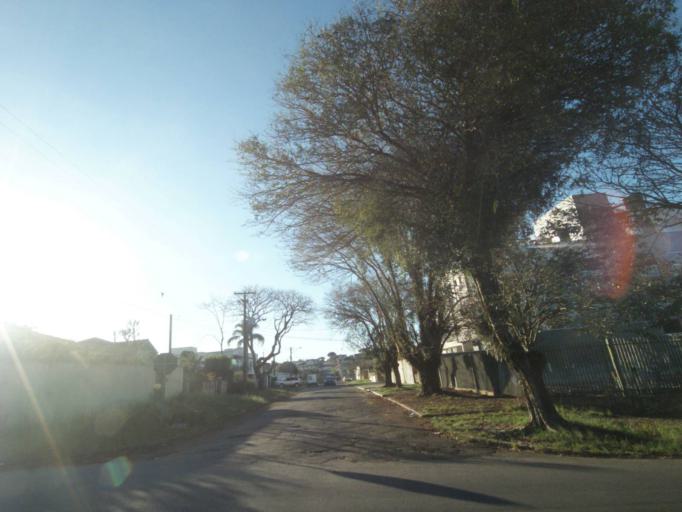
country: BR
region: Parana
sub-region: Curitiba
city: Curitiba
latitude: -25.3877
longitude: -49.2505
